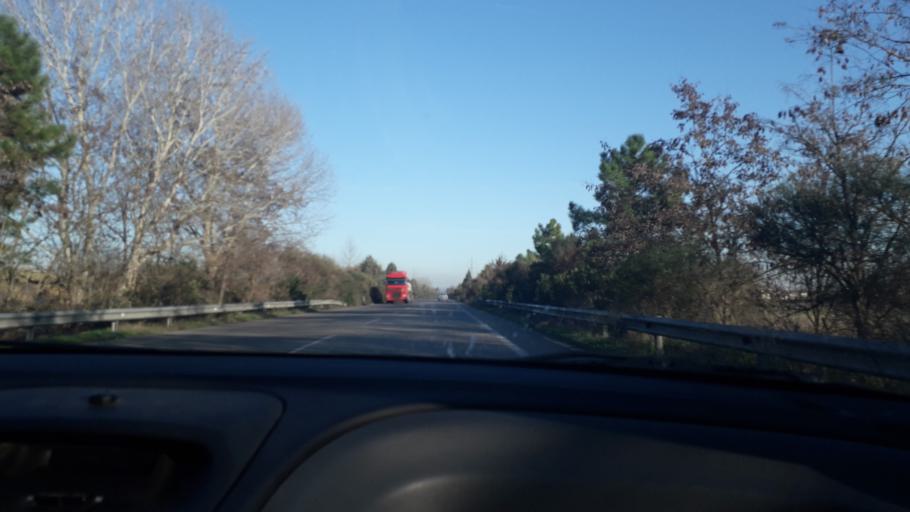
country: GR
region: Central Macedonia
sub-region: Nomos Pellis
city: Melissi
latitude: 40.7779
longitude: 22.3402
